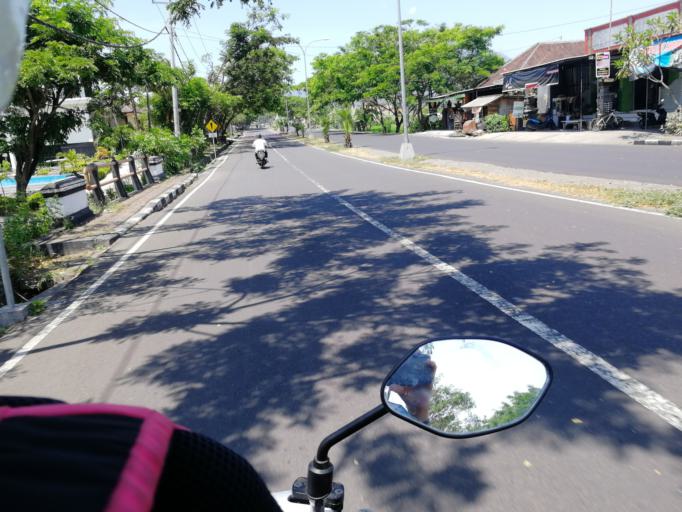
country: ID
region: Bali
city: Banjar Beji
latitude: -8.4442
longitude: 115.5897
